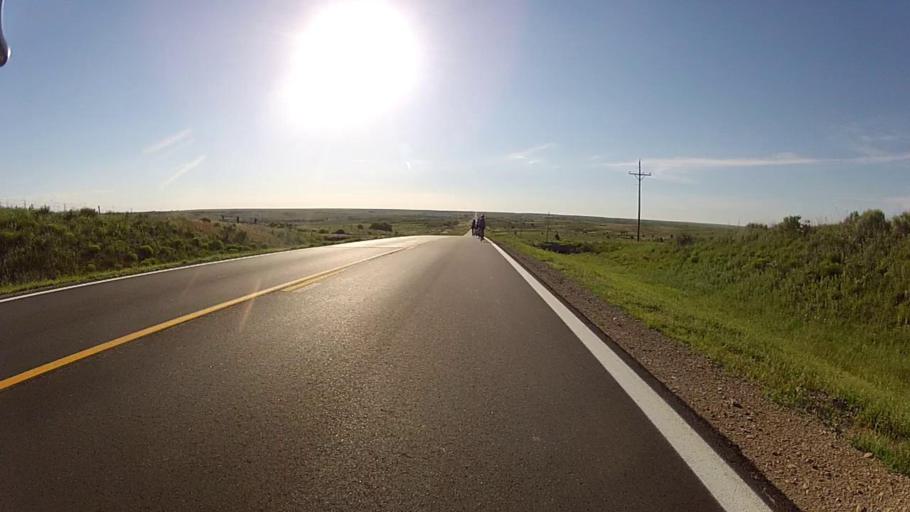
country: US
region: Kansas
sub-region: Comanche County
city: Coldwater
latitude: 37.2817
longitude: -99.0664
